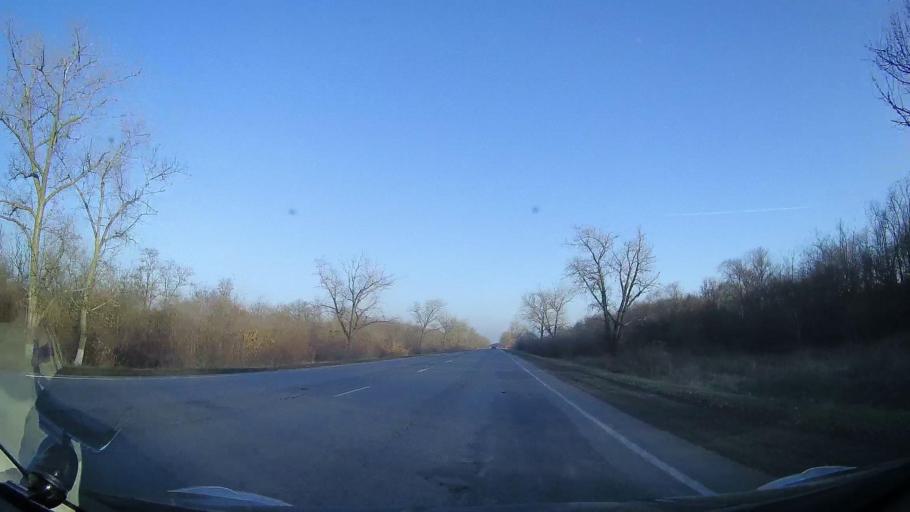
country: RU
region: Rostov
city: Kirovskaya
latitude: 47.0105
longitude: 39.9389
